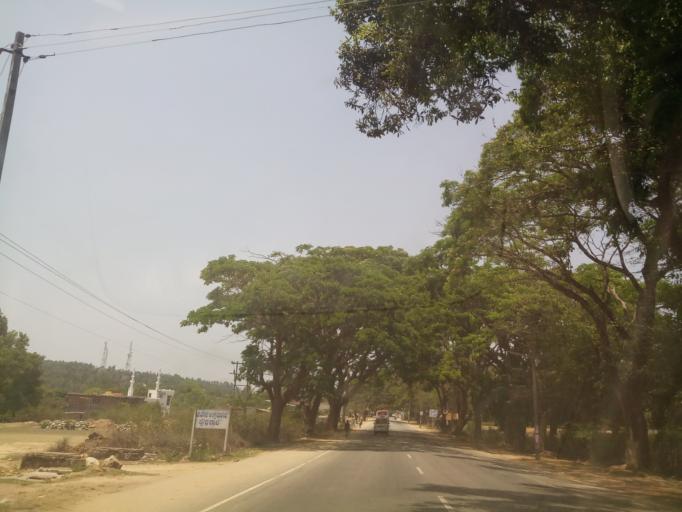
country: IN
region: Karnataka
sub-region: Hassan
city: Alur
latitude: 12.9449
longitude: 75.8883
